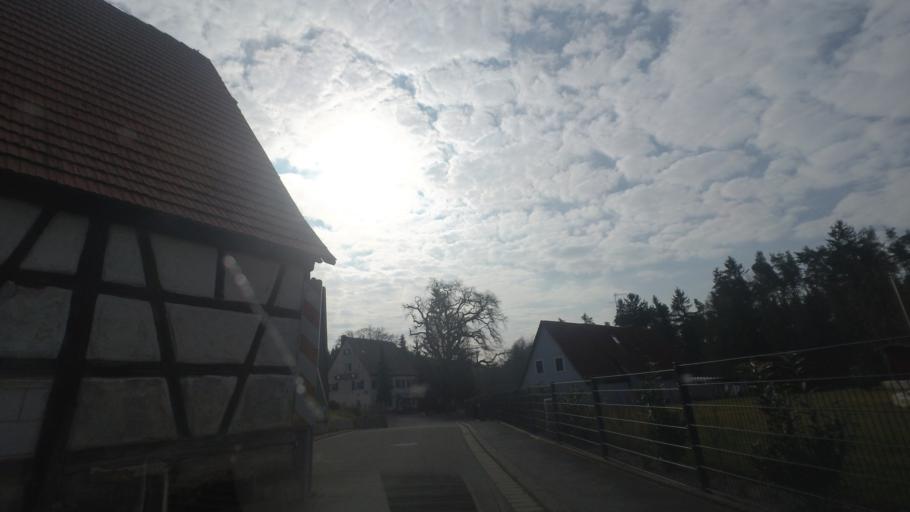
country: DE
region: Bavaria
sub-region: Regierungsbezirk Mittelfranken
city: Winkelhaid
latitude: 49.4100
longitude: 11.2978
